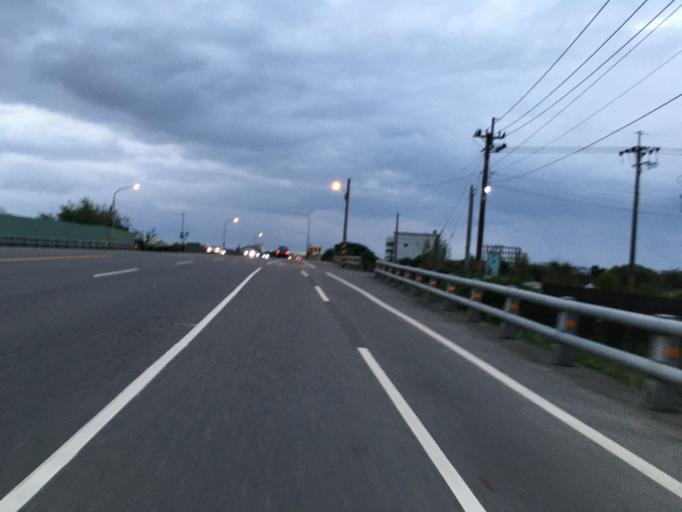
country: TW
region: Taiwan
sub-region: Yilan
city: Yilan
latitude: 24.6303
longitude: 121.8320
